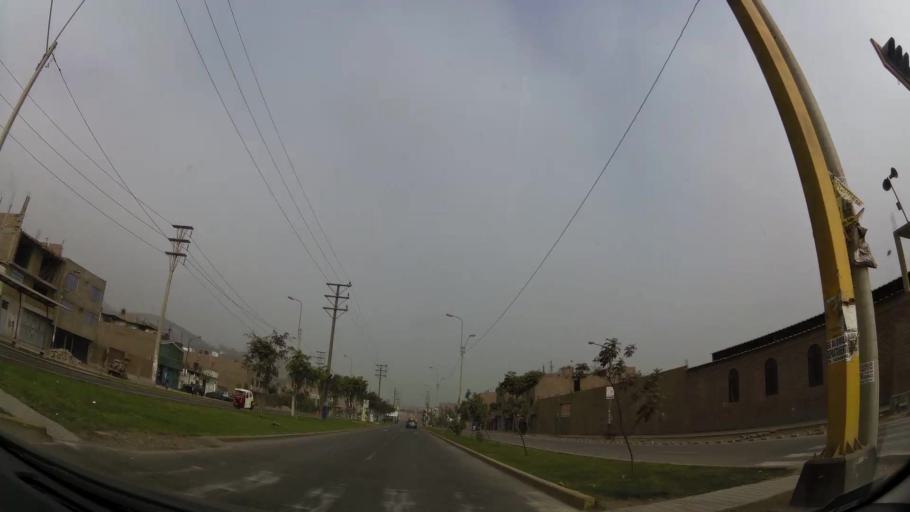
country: PE
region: Lima
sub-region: Lima
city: Santa Maria
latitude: -11.9992
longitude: -76.8339
